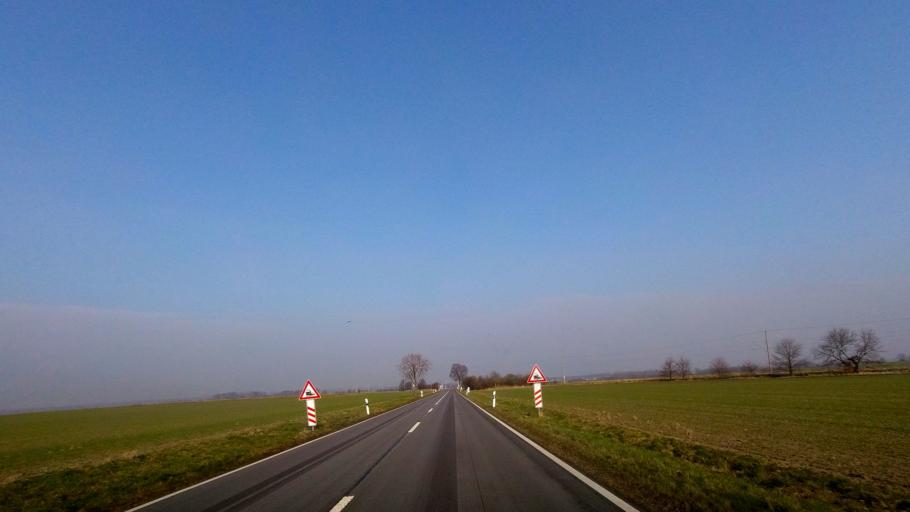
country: DE
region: Brandenburg
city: Niedergorsdorf
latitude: 51.9478
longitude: 13.0394
